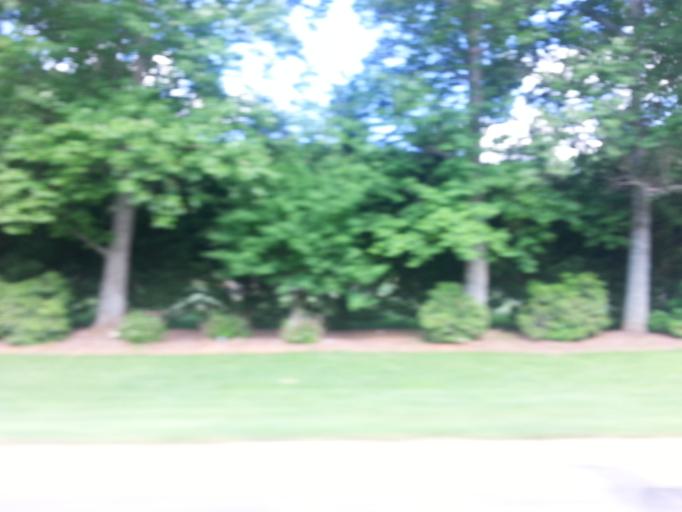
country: US
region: Georgia
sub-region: Towns County
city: Hiawassee
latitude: 34.8918
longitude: -83.7193
